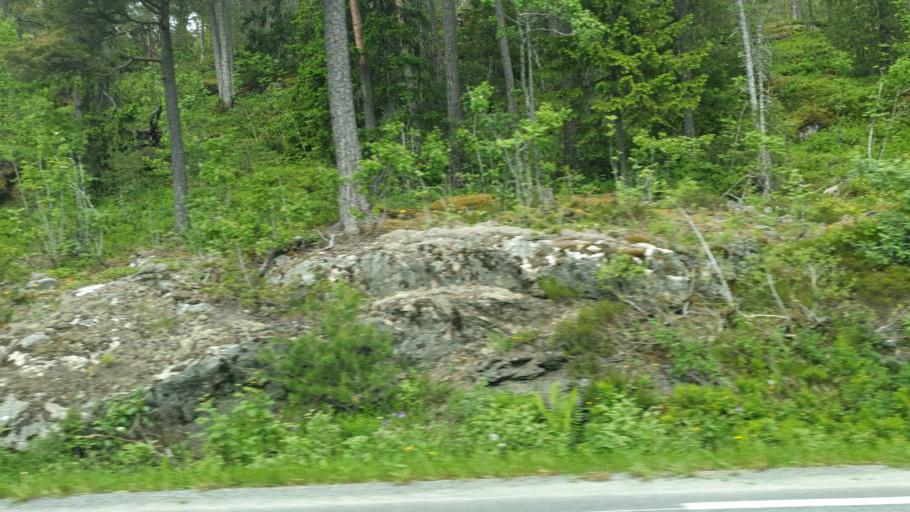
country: NO
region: Sor-Trondelag
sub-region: Trondheim
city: Trondheim
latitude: 63.5583
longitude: 10.3122
